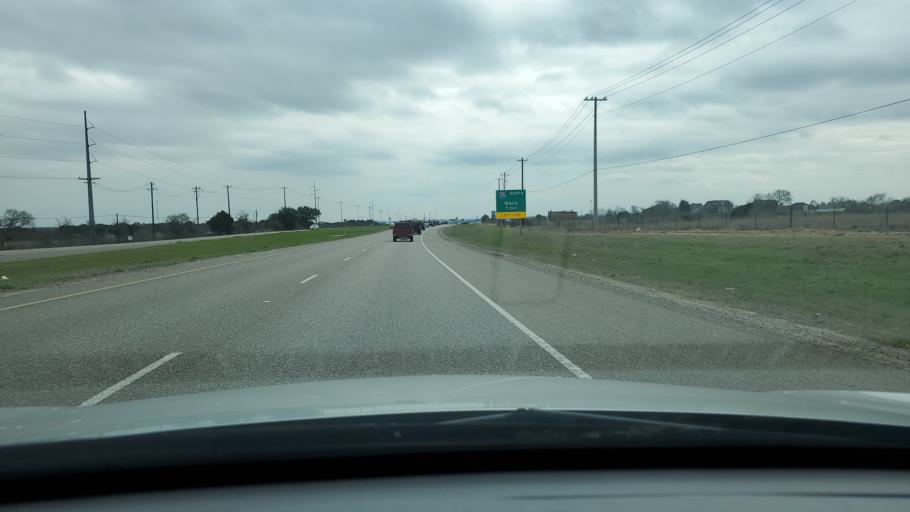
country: US
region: Texas
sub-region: Williamson County
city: Serenada
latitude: 30.7197
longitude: -97.6658
